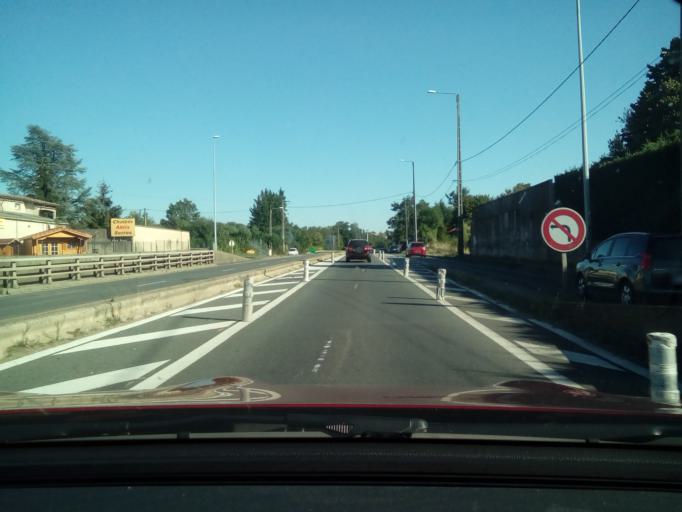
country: FR
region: Rhone-Alpes
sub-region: Departement du Rhone
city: Limonest
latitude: 45.8336
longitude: 4.7493
